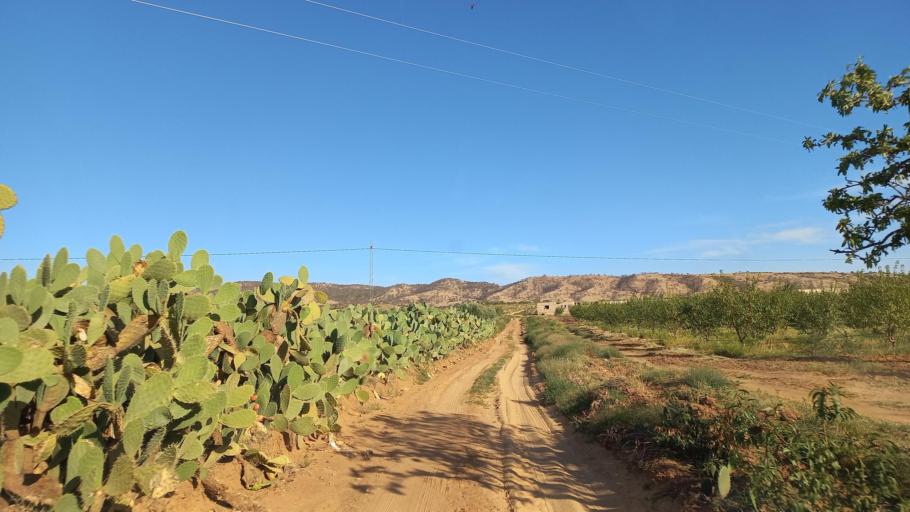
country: TN
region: Al Qasrayn
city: Sbiba
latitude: 35.3351
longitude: 9.1267
